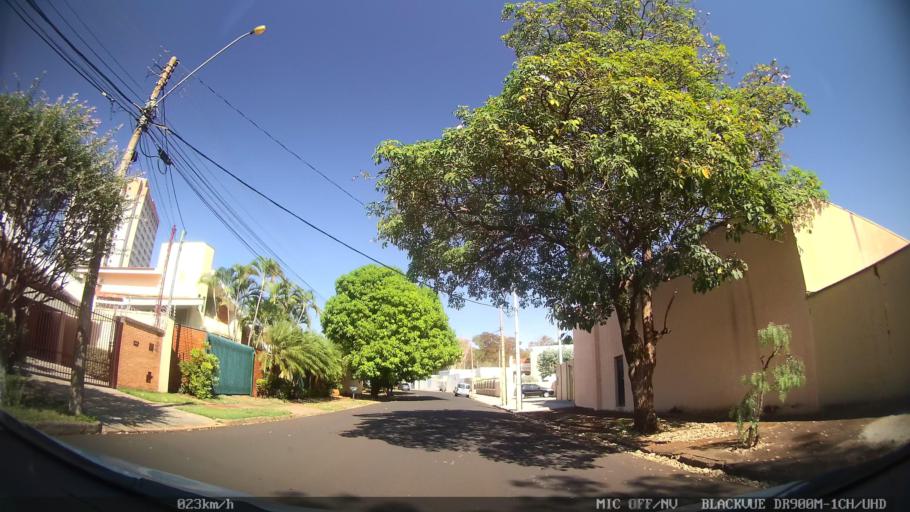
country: BR
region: Sao Paulo
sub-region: Ribeirao Preto
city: Ribeirao Preto
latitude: -21.2003
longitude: -47.7767
